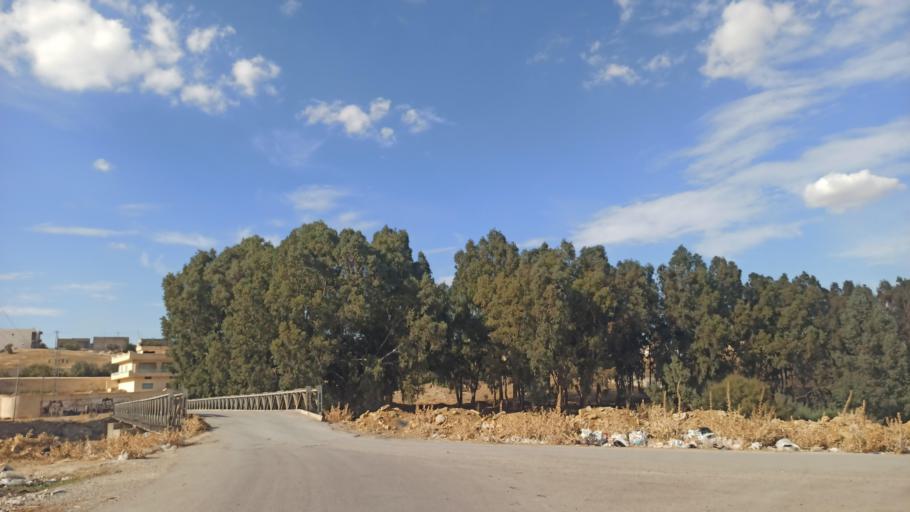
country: TN
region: Zaghwan
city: Zaghouan
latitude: 36.3441
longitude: 10.2077
